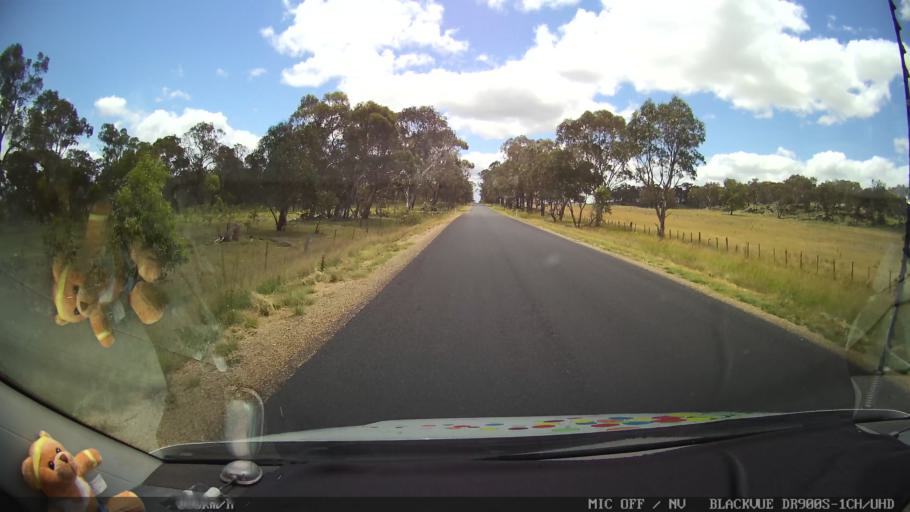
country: AU
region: New South Wales
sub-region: Glen Innes Severn
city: Glen Innes
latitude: -29.4234
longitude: 151.7080
